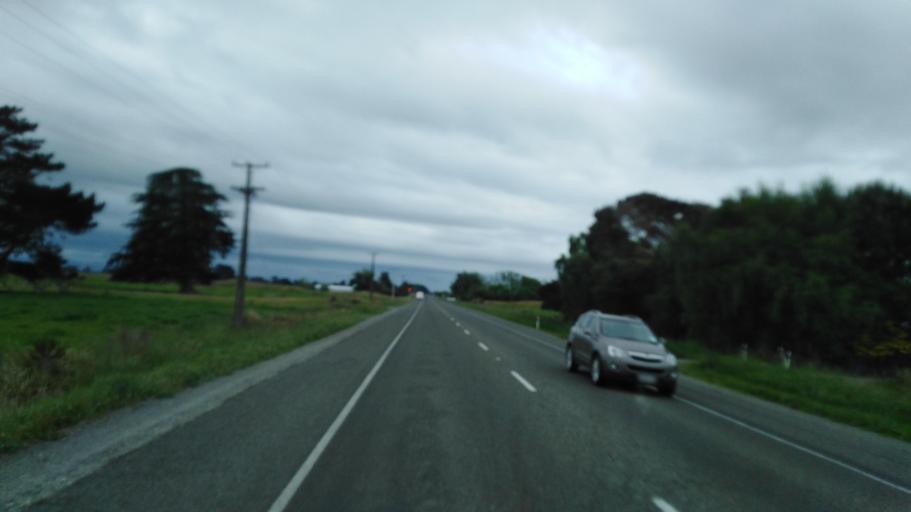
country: NZ
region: Manawatu-Wanganui
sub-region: Horowhenua District
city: Foxton
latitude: -40.3710
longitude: 175.3216
